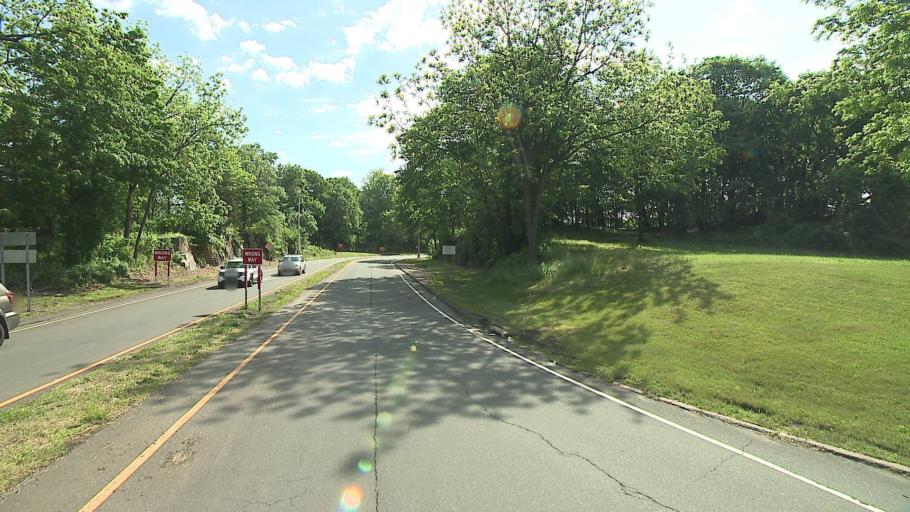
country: US
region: Connecticut
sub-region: Fairfield County
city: Fairfield
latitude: 41.1452
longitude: -73.2659
